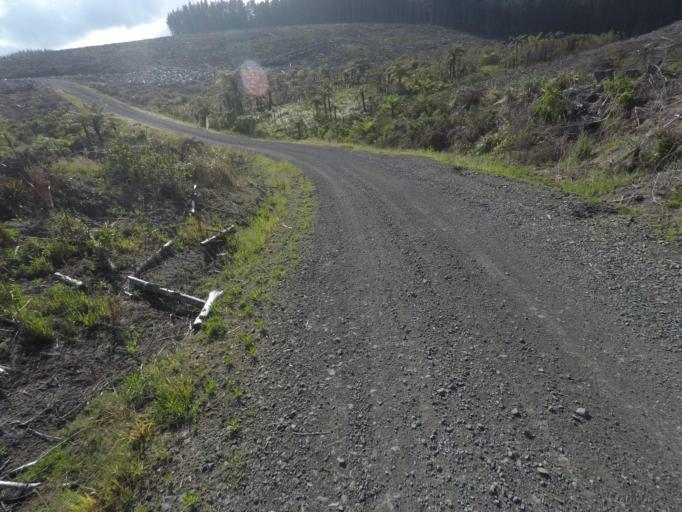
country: NZ
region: Auckland
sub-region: Auckland
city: Parakai
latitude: -36.7146
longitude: 174.5652
